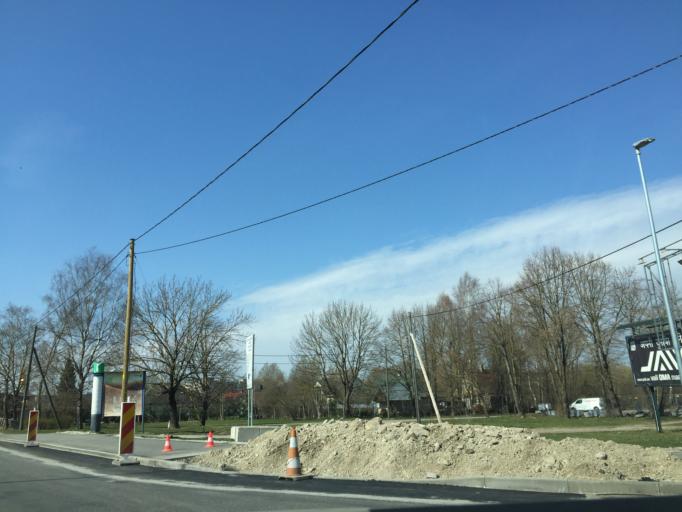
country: EE
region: Ida-Virumaa
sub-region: Narva linn
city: Narva
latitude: 59.3865
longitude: 28.1979
